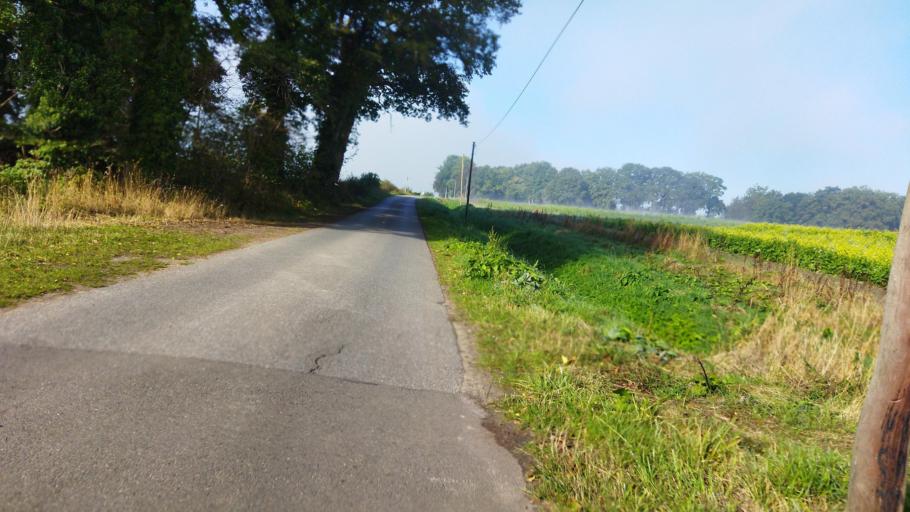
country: DE
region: North Rhine-Westphalia
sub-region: Regierungsbezirk Munster
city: Wettringen
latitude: 52.2255
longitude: 7.3261
